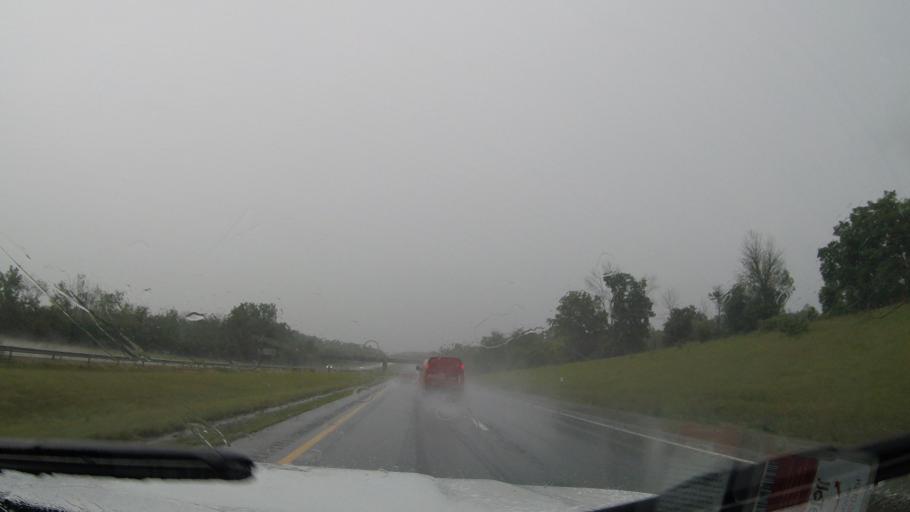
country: US
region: New York
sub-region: Seneca County
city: Seneca Falls
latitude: 42.9691
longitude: -76.8317
